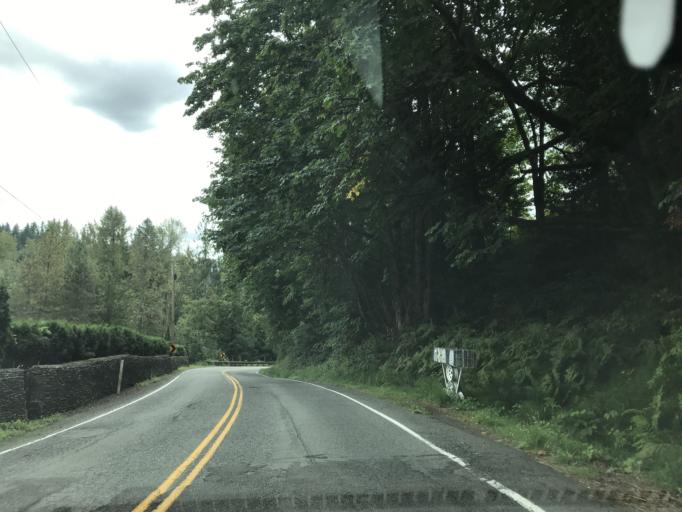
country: US
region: Washington
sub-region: King County
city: Black Diamond
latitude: 47.2829
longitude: -122.0384
